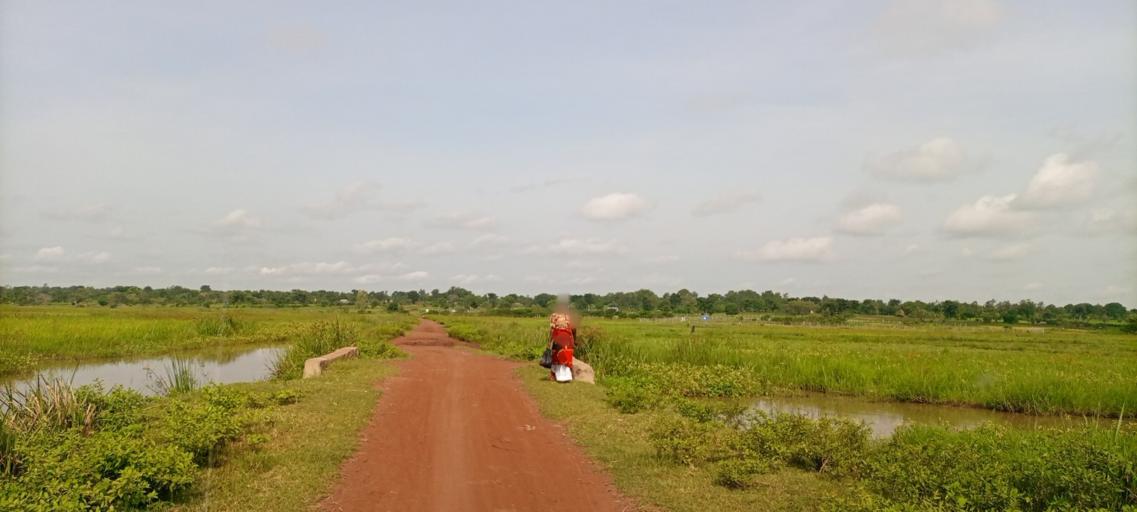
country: UG
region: Eastern Region
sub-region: Kibuku District
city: Kibuku
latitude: 1.0989
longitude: 33.7729
